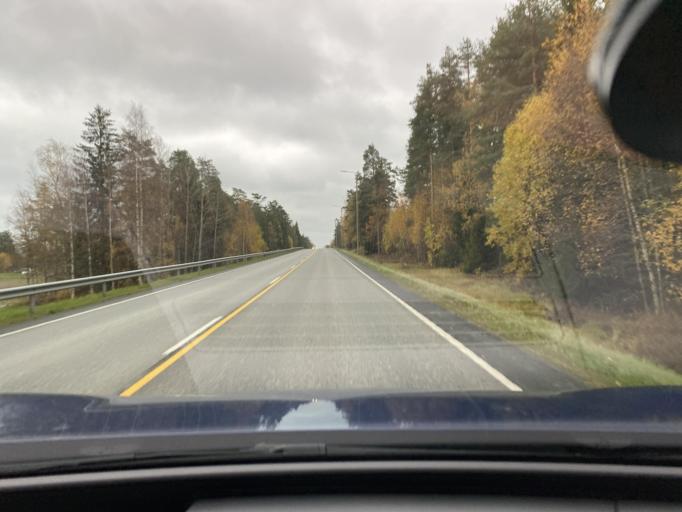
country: FI
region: Varsinais-Suomi
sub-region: Vakka-Suomi
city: Laitila
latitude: 60.9688
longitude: 21.5939
